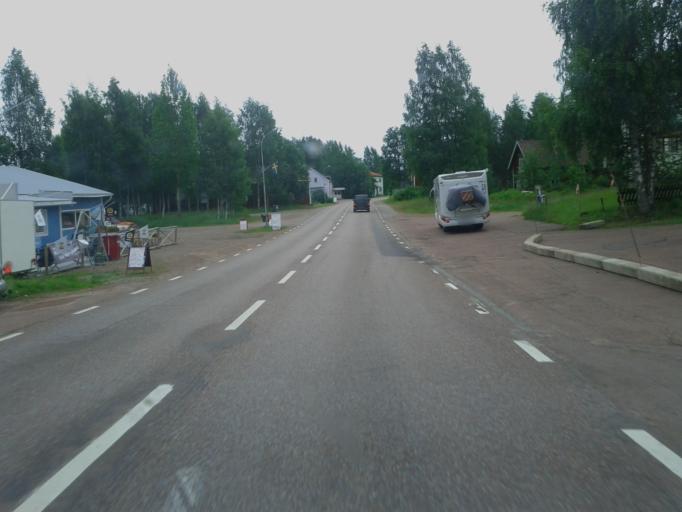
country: NO
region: Hedmark
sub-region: Trysil
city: Innbygda
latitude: 61.6948
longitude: 13.1327
